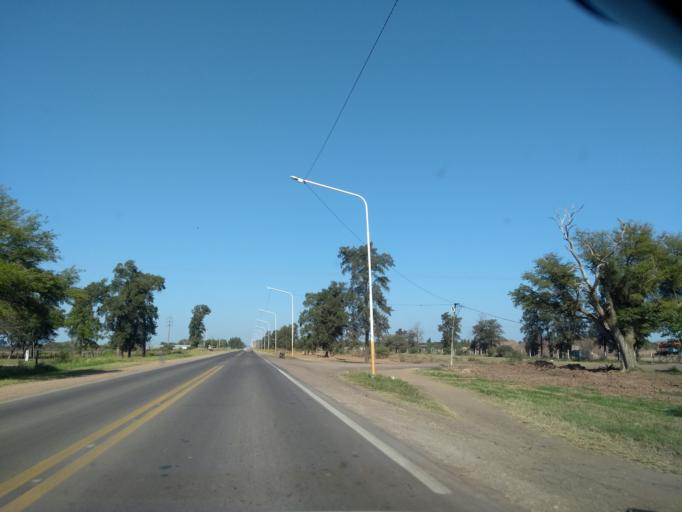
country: AR
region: Chaco
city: Presidencia Roque Saenz Pena
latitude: -26.7820
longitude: -60.4050
